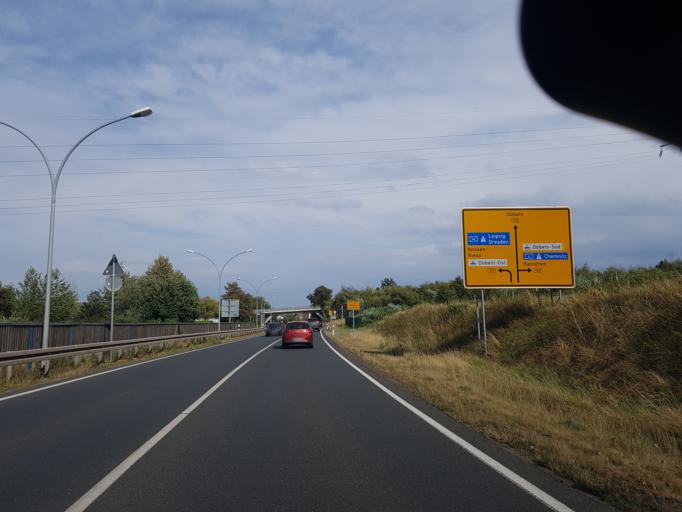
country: DE
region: Saxony
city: Dobeln
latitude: 51.1250
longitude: 13.0894
